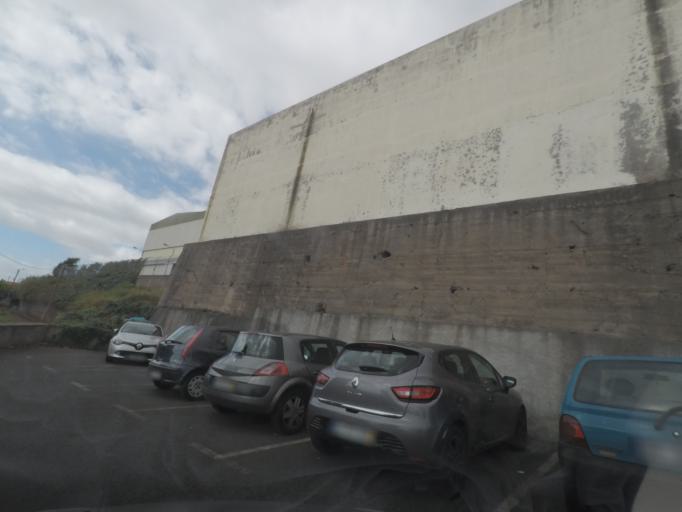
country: PT
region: Madeira
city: Camara de Lobos
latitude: 32.6552
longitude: -16.9469
